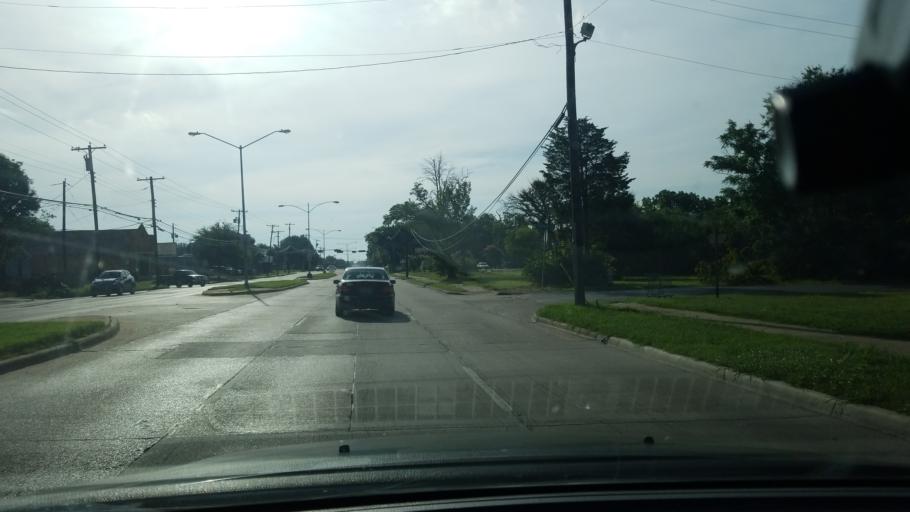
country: US
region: Texas
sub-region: Dallas County
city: Balch Springs
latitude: 32.7487
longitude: -96.6810
